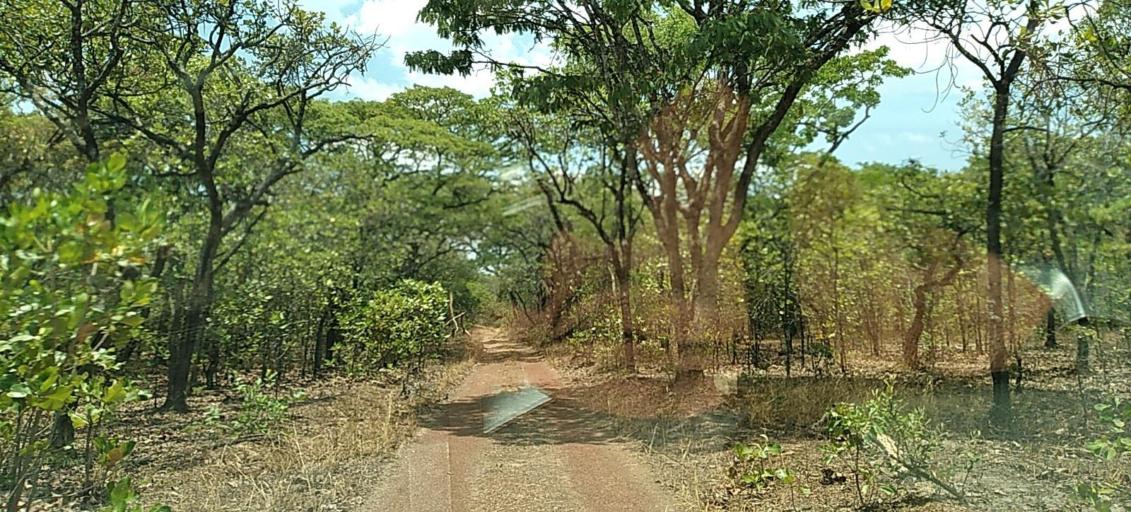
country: ZM
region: Copperbelt
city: Chililabombwe
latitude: -12.4607
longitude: 27.6988
